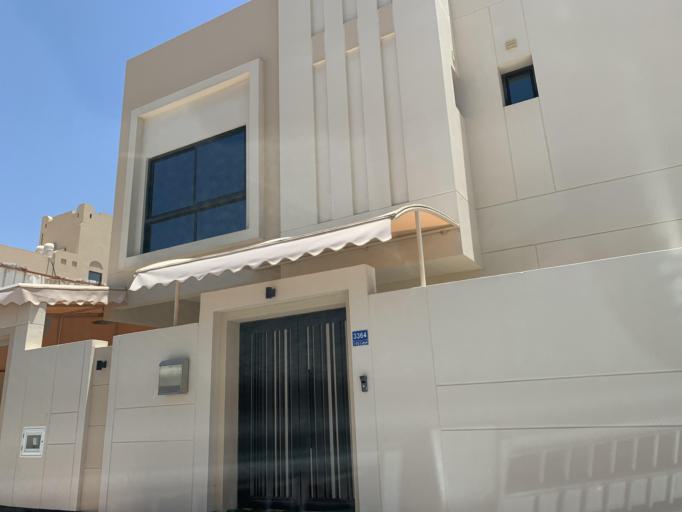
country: BH
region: Manama
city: Jidd Hafs
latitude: 26.2324
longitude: 50.4977
